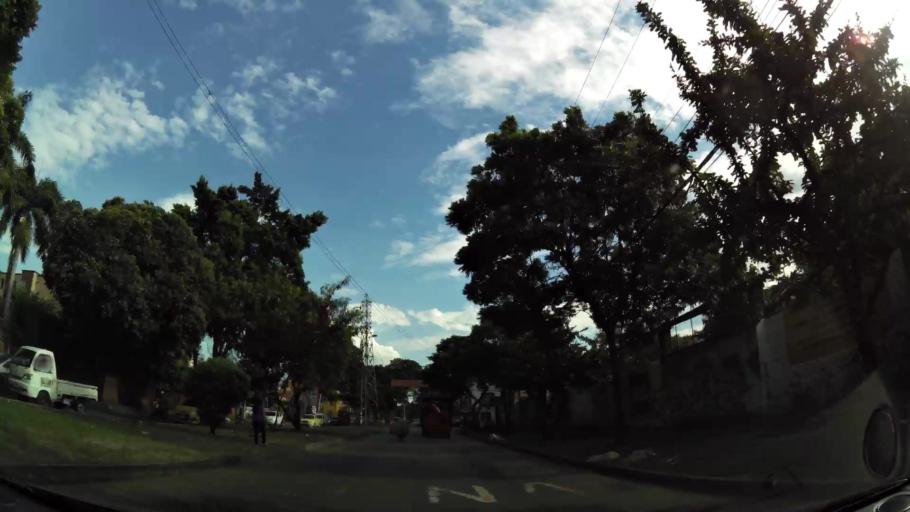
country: CO
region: Valle del Cauca
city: Cali
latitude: 3.4637
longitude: -76.5080
